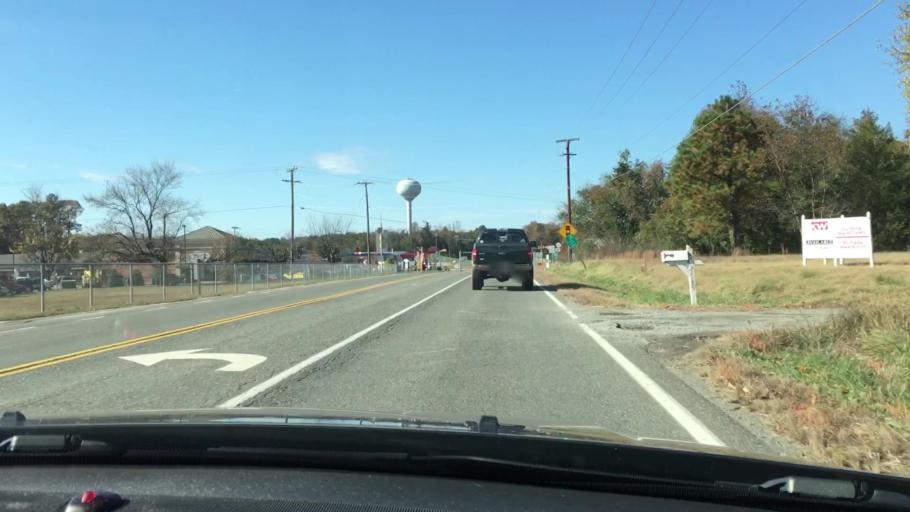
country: US
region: Virginia
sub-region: King William County
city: Central Garage
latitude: 37.7434
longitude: -77.1301
